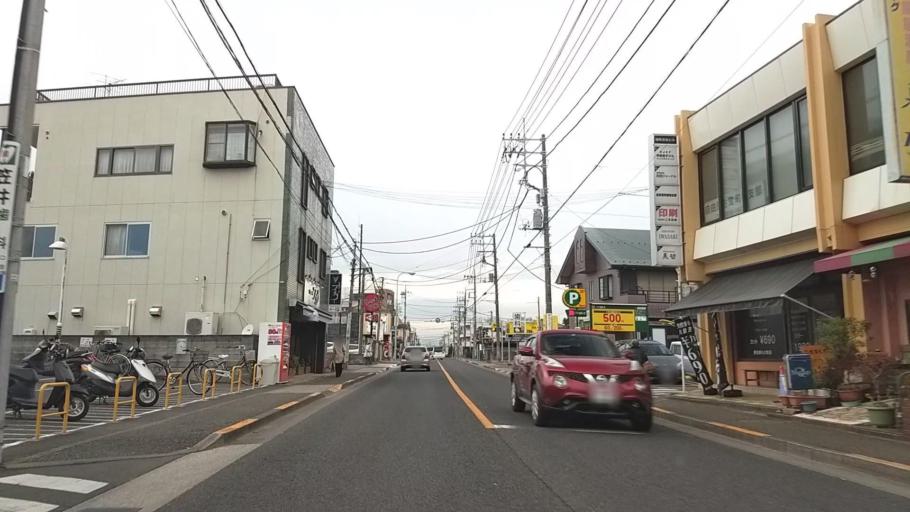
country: JP
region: Tokyo
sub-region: Machida-shi
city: Machida
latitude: 35.5549
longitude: 139.4366
